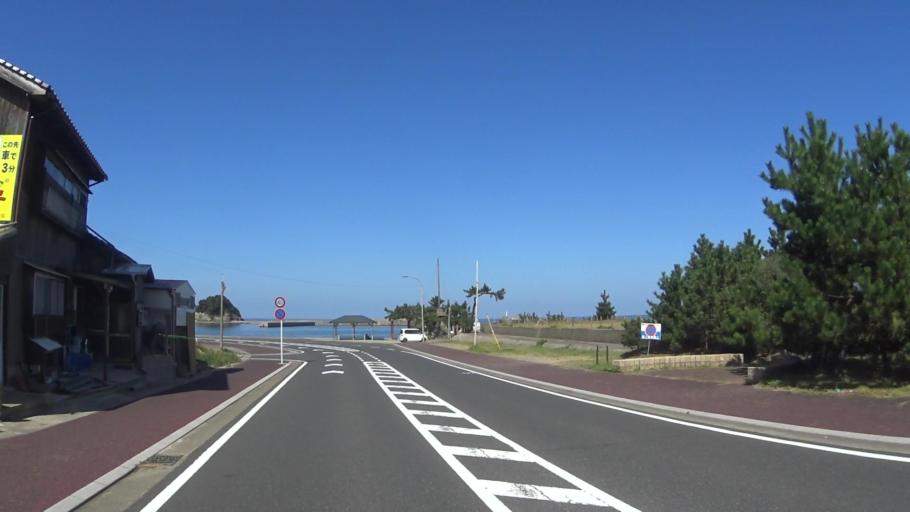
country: JP
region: Kyoto
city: Miyazu
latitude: 35.6907
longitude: 135.0186
